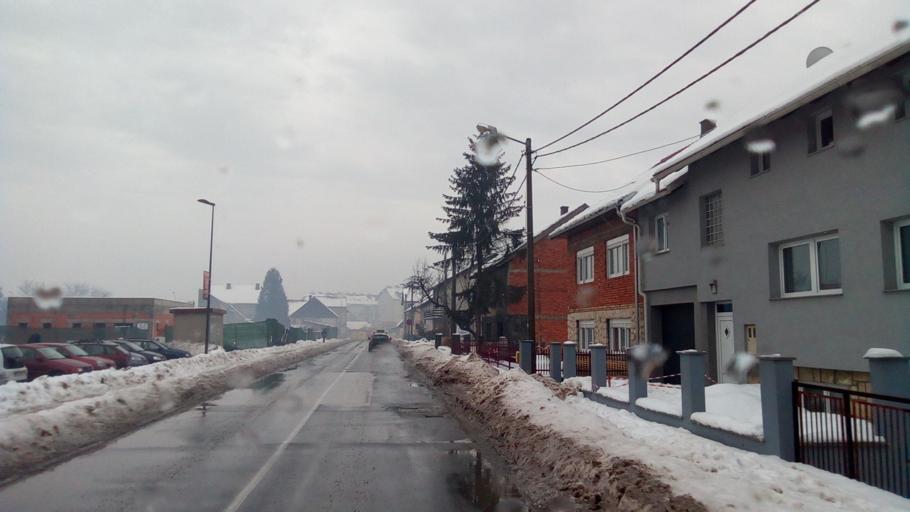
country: HR
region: Sisacko-Moslavacka
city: Petrinja
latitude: 45.4415
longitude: 16.2678
